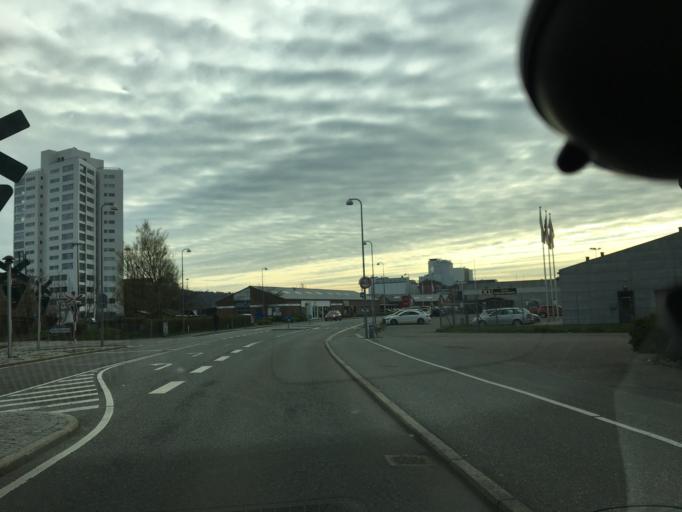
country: DK
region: South Denmark
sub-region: Vejle Kommune
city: Vejle
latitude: 55.7047
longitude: 9.5385
